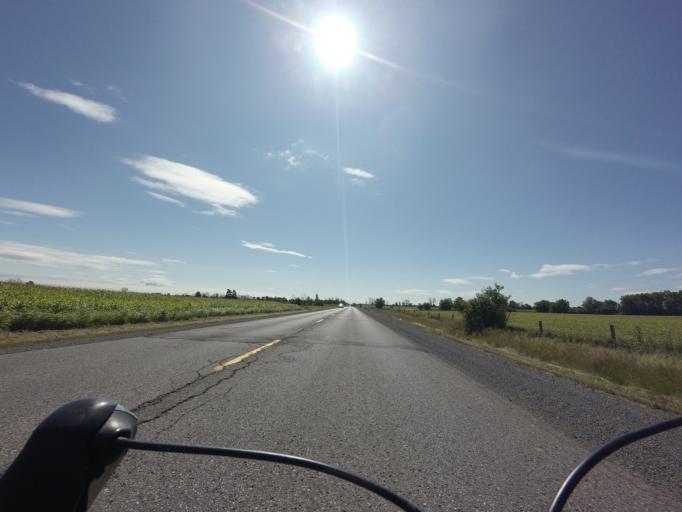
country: CA
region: Ontario
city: Bells Corners
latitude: 45.2179
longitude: -75.8301
